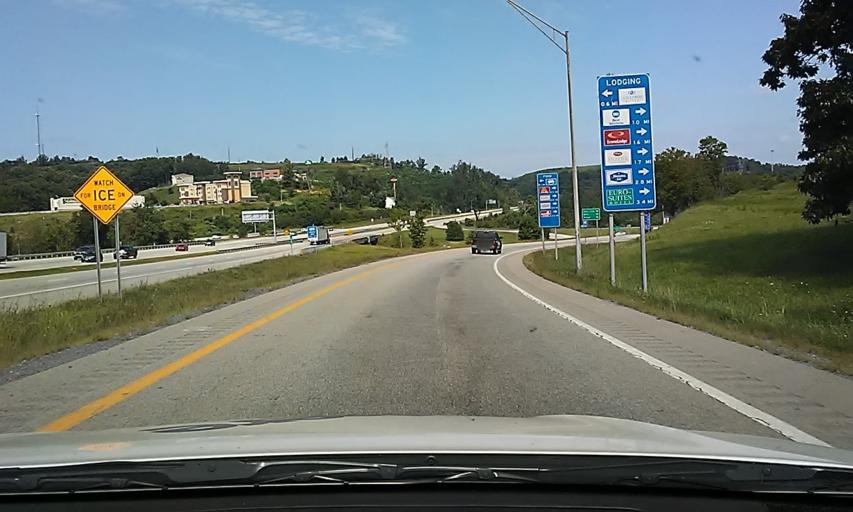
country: US
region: West Virginia
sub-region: Monongalia County
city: Star City
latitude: 39.6529
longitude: -80.0089
